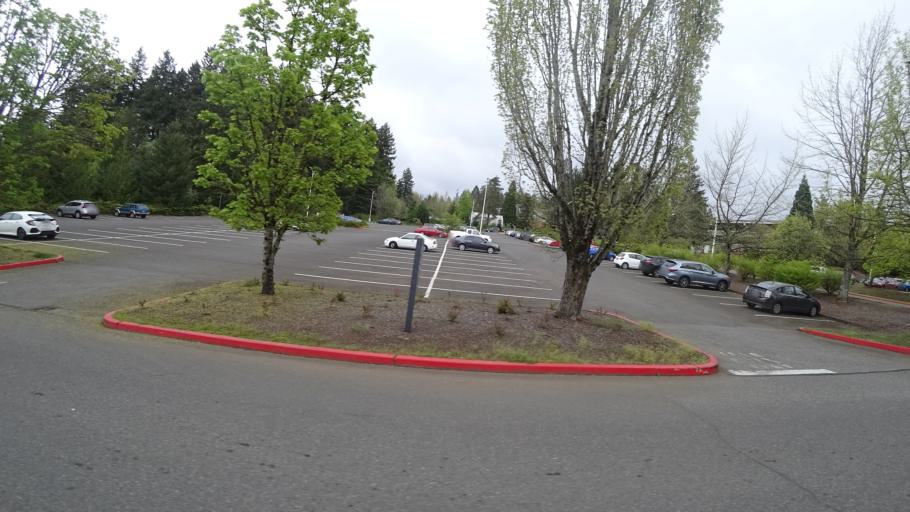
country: US
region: Oregon
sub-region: Washington County
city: Metzger
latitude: 45.4402
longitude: -122.7339
